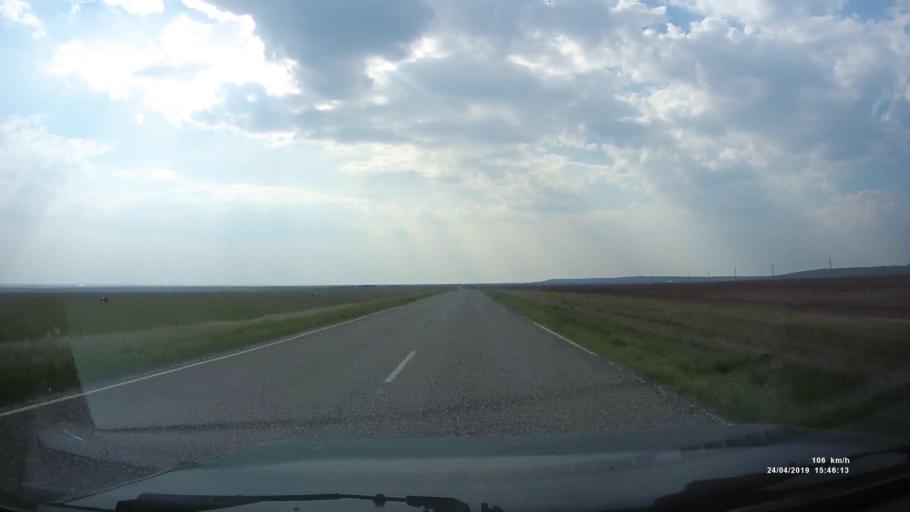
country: RU
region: Kalmykiya
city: Yashalta
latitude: 46.5925
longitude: 42.7198
